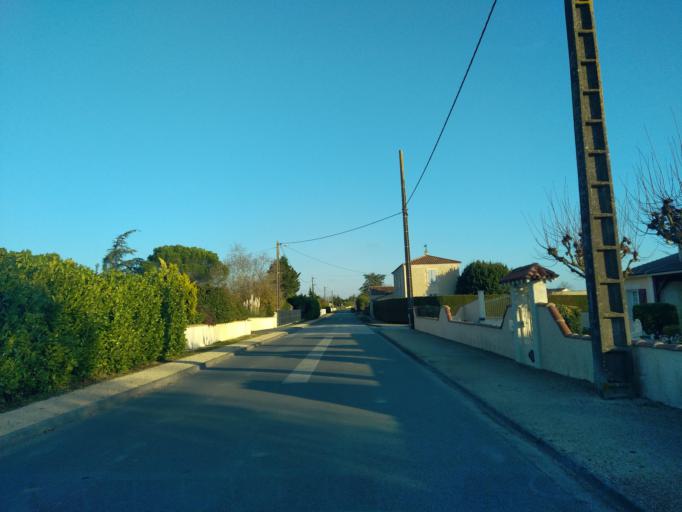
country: FR
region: Pays de la Loire
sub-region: Departement de la Vendee
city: Maillezais
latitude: 46.3416
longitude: -0.7810
